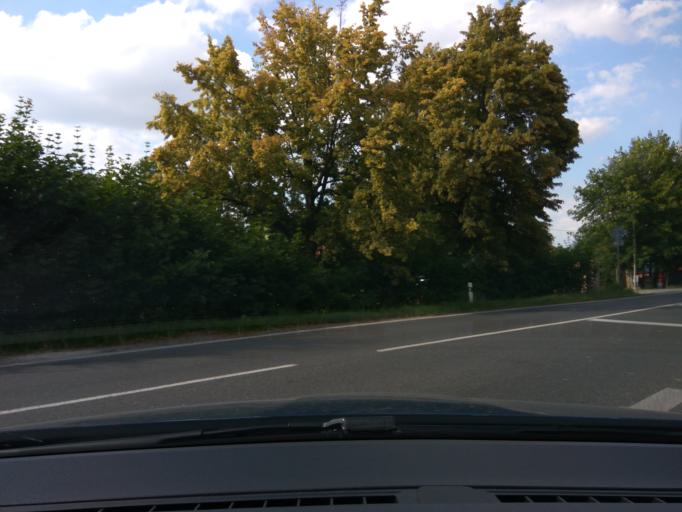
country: CZ
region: Praha
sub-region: Praha 19
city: Satalice
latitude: 50.1401
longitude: 14.5758
